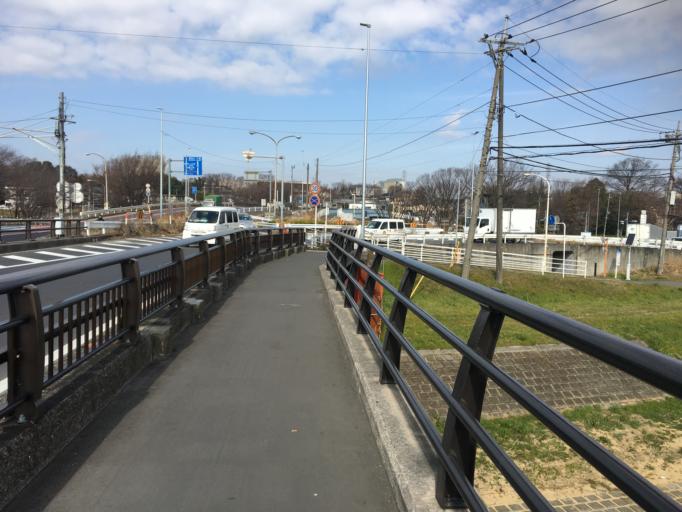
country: JP
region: Saitama
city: Shiki
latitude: 35.8137
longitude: 139.5477
